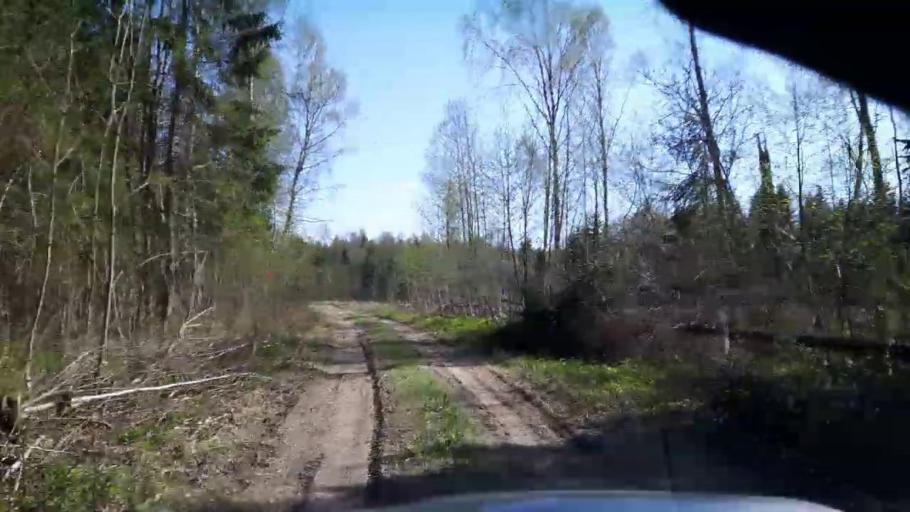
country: EE
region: Paernumaa
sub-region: Tootsi vald
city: Tootsi
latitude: 58.5433
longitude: 24.8027
